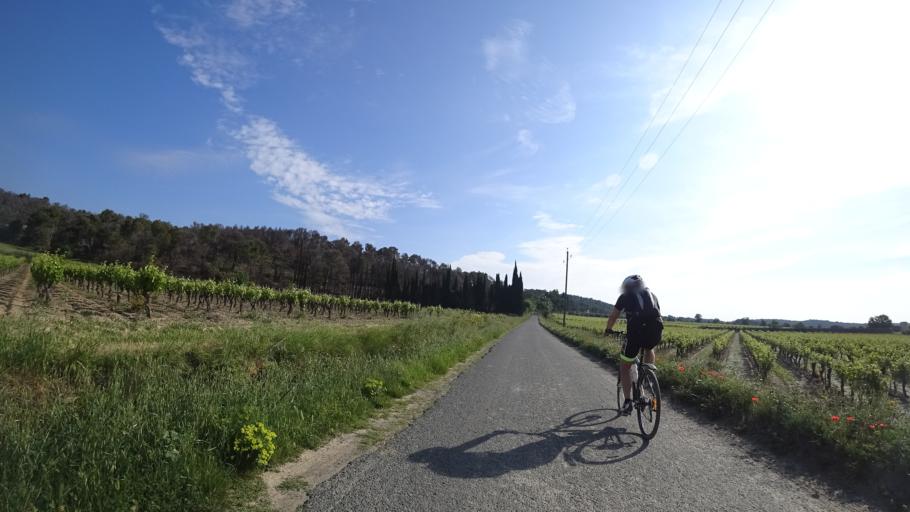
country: FR
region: Languedoc-Roussillon
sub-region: Departement de l'Herault
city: Olonzac
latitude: 43.2406
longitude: 2.7157
